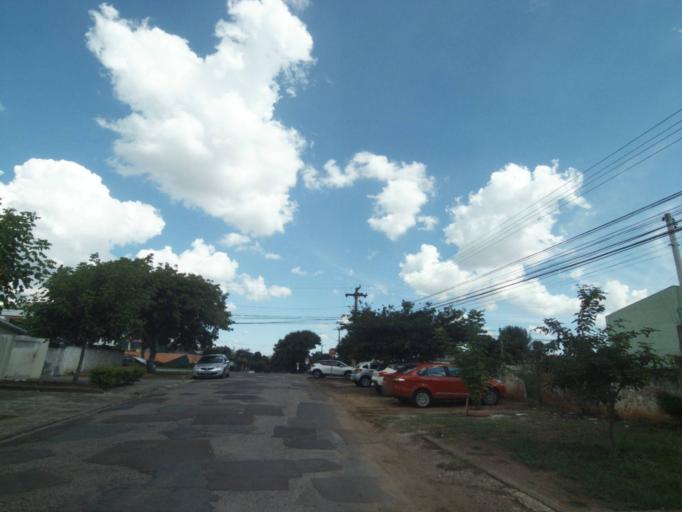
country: BR
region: Parana
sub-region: Pinhais
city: Pinhais
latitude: -25.4544
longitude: -49.2103
